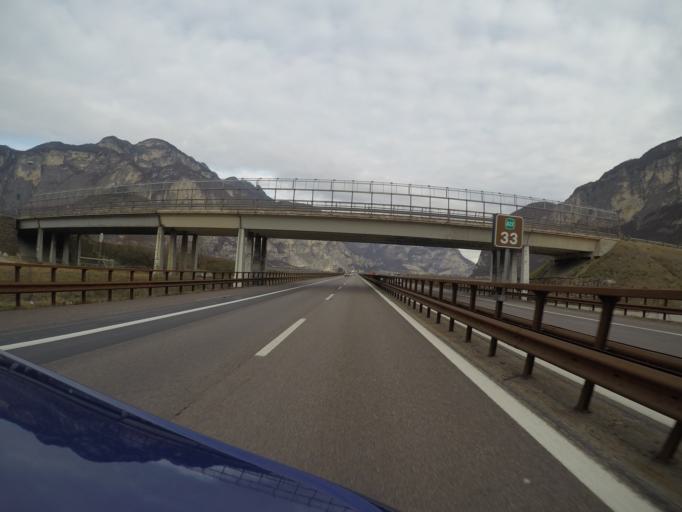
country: IT
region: Trentino-Alto Adige
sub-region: Provincia di Trento
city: Mezzocorona
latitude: 46.2059
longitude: 11.1367
